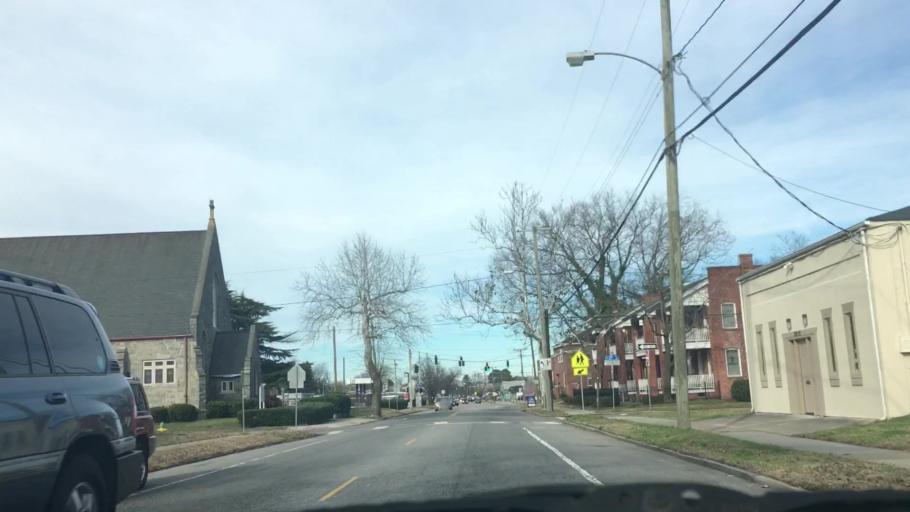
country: US
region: Virginia
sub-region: City of Norfolk
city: Norfolk
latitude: 36.8788
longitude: -76.2947
